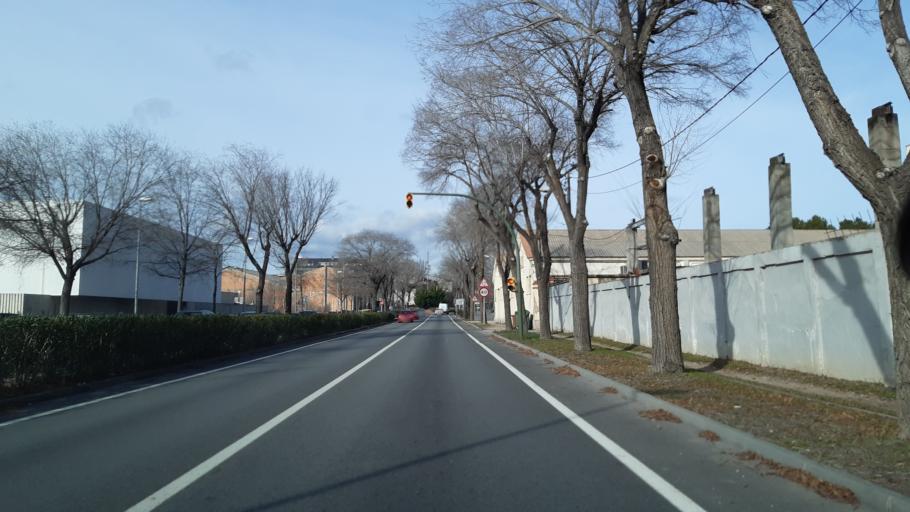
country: ES
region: Catalonia
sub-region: Provincia de Barcelona
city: Vilanova del Cami
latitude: 41.5738
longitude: 1.6429
